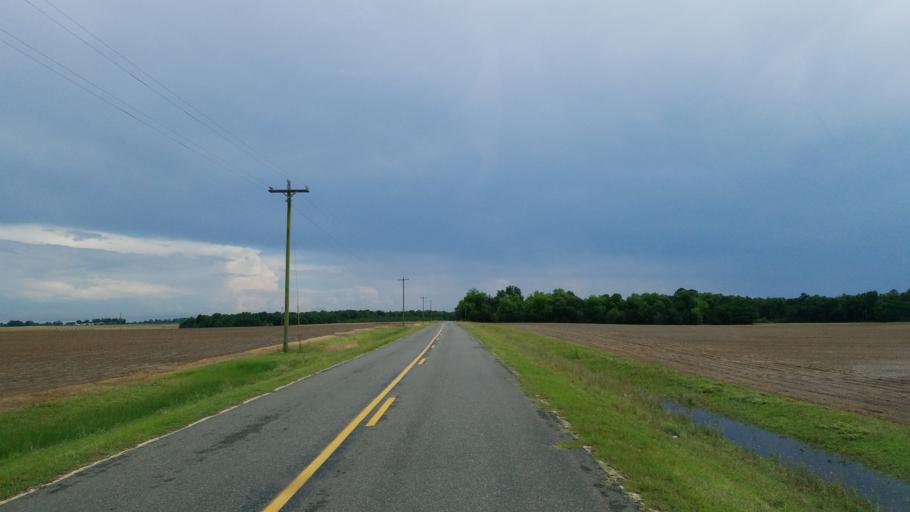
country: US
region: Georgia
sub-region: Dooly County
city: Unadilla
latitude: 32.2785
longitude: -83.7954
